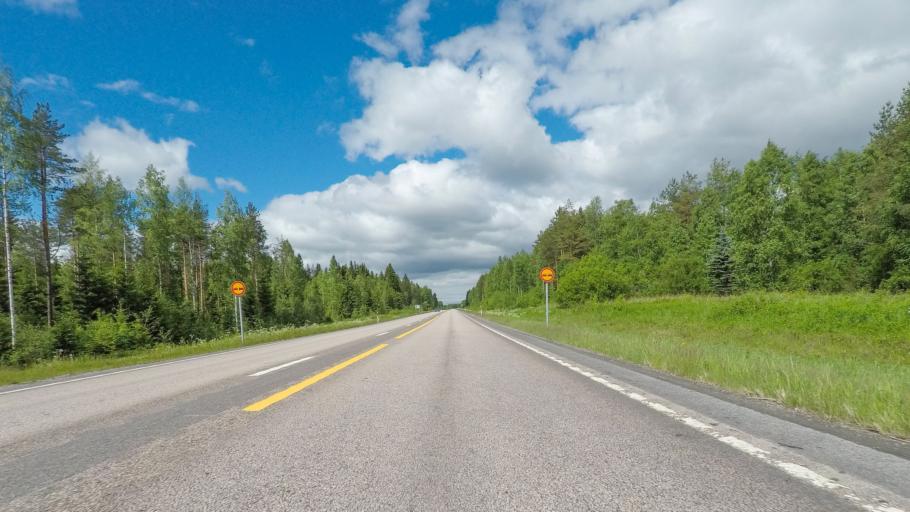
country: FI
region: Paijanne Tavastia
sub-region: Lahti
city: Hartola
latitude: 61.4008
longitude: 26.0466
